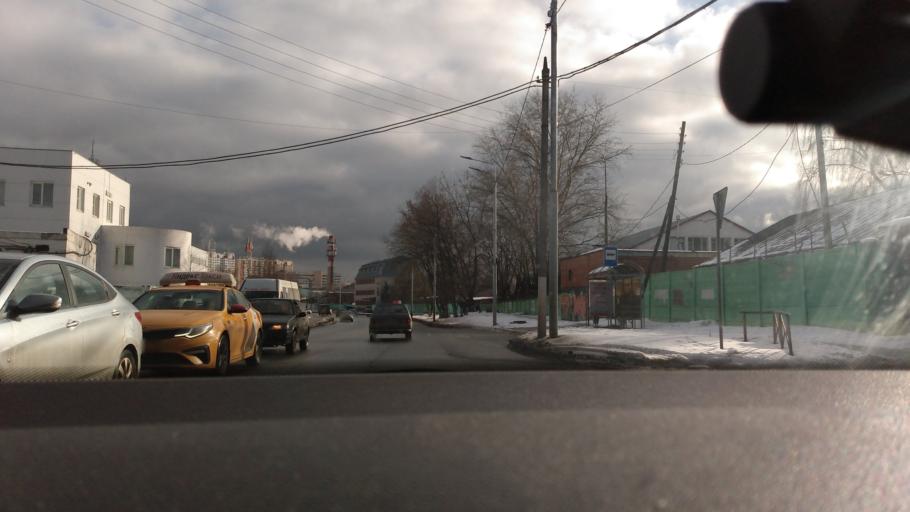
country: RU
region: Moskovskaya
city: Balashikha
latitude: 55.8336
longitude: 37.9457
